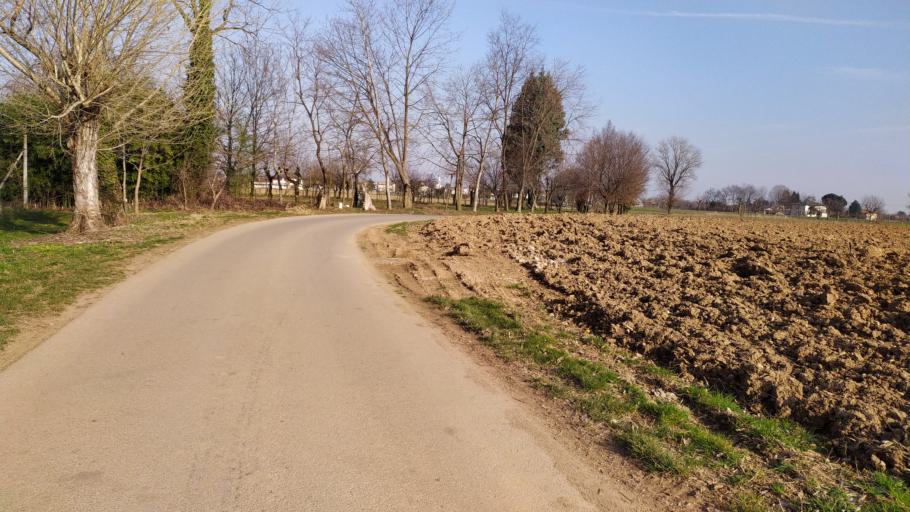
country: IT
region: Veneto
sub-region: Provincia di Vicenza
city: Giavenale
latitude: 45.6915
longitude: 11.4112
